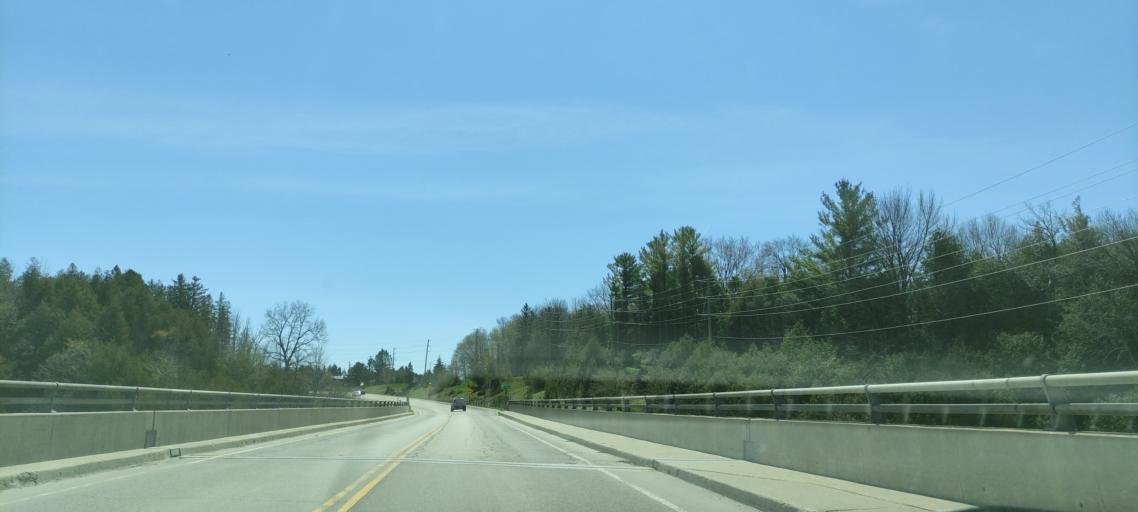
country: CA
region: Ontario
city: Waterloo
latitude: 43.5884
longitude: -80.4710
